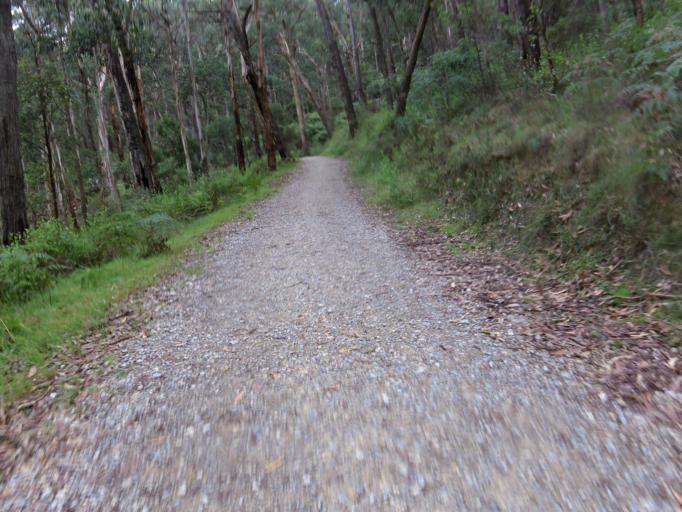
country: AU
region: Victoria
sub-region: Knox
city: The Basin
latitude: -37.8415
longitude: 145.3396
